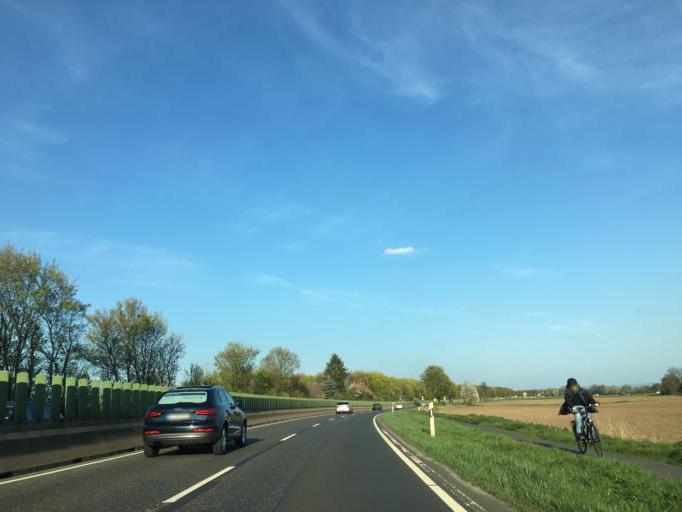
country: DE
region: Hesse
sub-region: Regierungsbezirk Darmstadt
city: Offenbach
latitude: 50.1392
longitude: 8.7856
